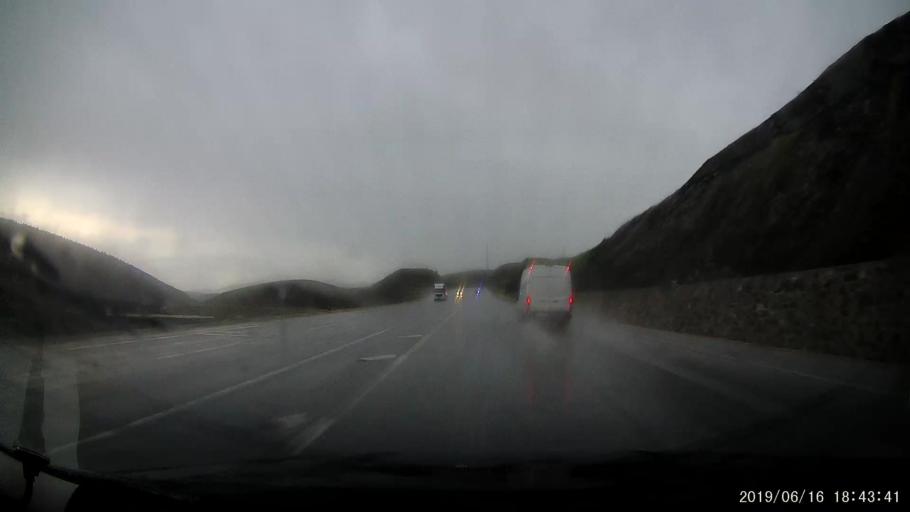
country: TR
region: Erzincan
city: Doganbeyli
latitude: 39.8718
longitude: 39.0885
